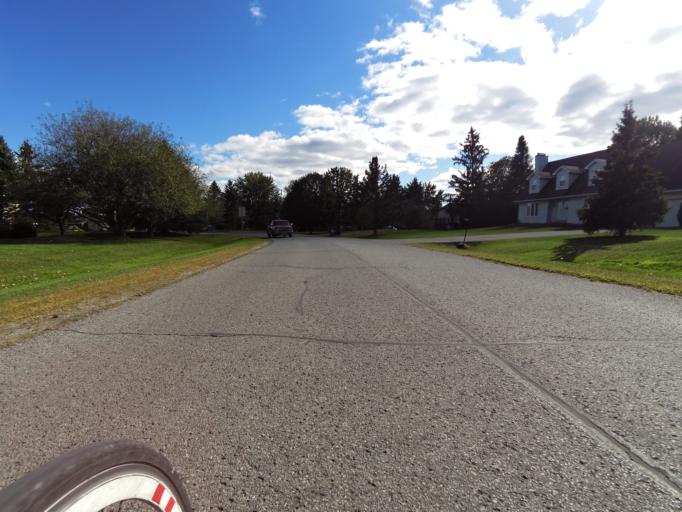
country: CA
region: Ontario
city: Bells Corners
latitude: 45.1556
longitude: -75.6558
